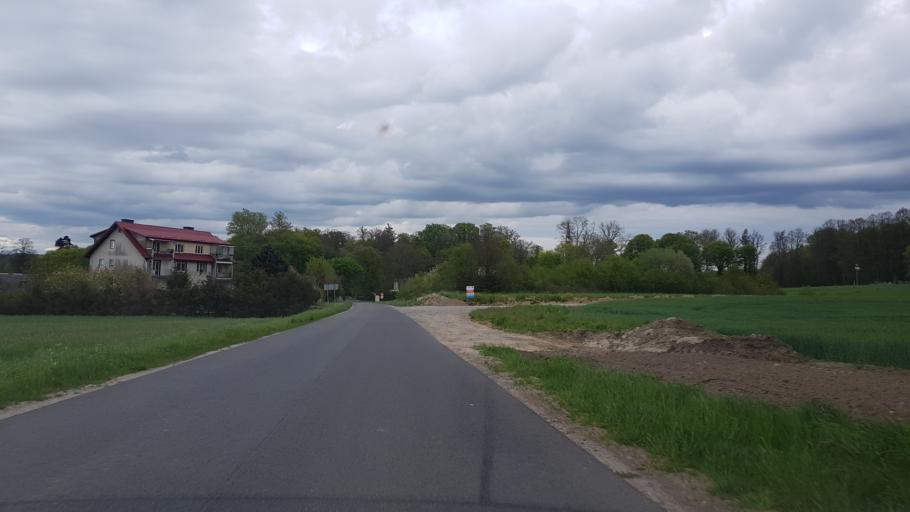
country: PL
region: West Pomeranian Voivodeship
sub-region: Powiat slawienski
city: Slawno
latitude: 54.2727
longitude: 16.5468
